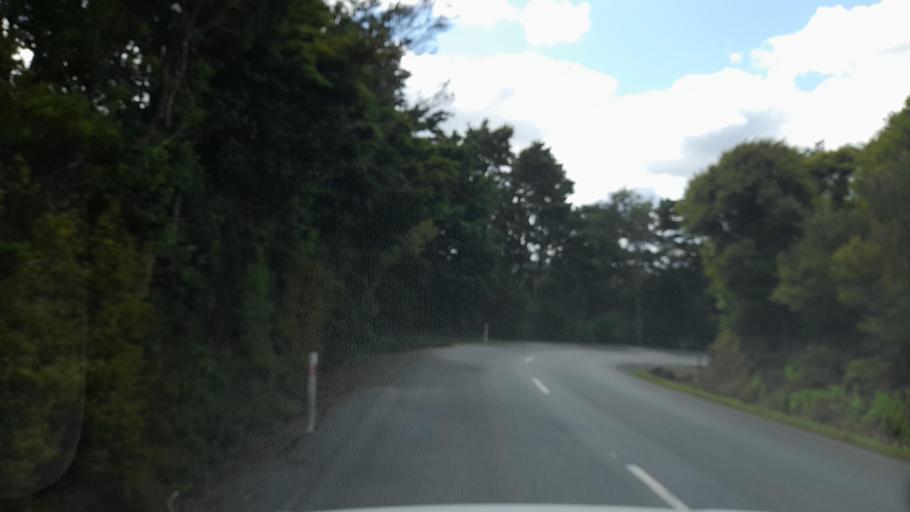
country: NZ
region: Northland
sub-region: Whangarei
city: Maungatapere
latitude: -35.6712
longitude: 174.0394
